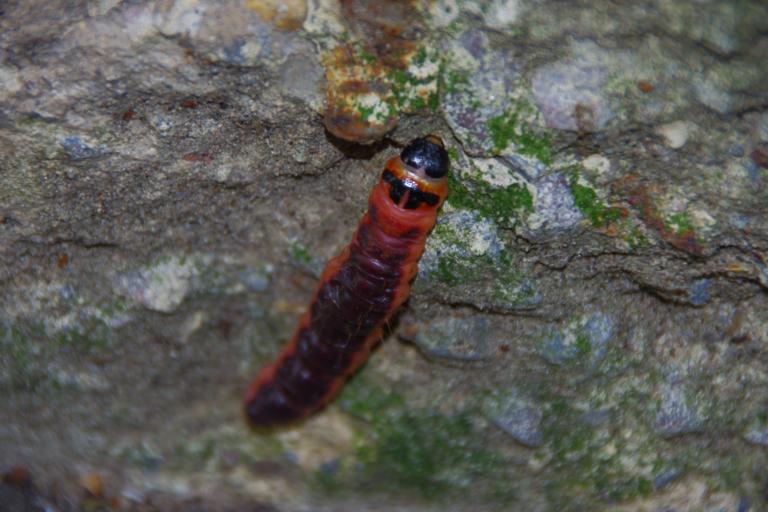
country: RU
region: Moskovskaya
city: Krasnogorsk
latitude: 55.8360
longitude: 37.3018
